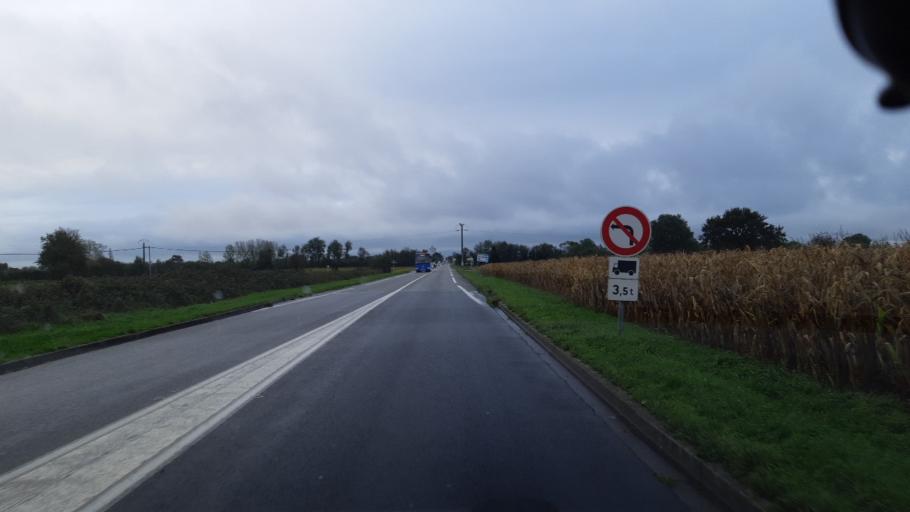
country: FR
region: Lower Normandy
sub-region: Departement de la Manche
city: Donville-les-Bains
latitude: 48.8627
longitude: -1.5467
